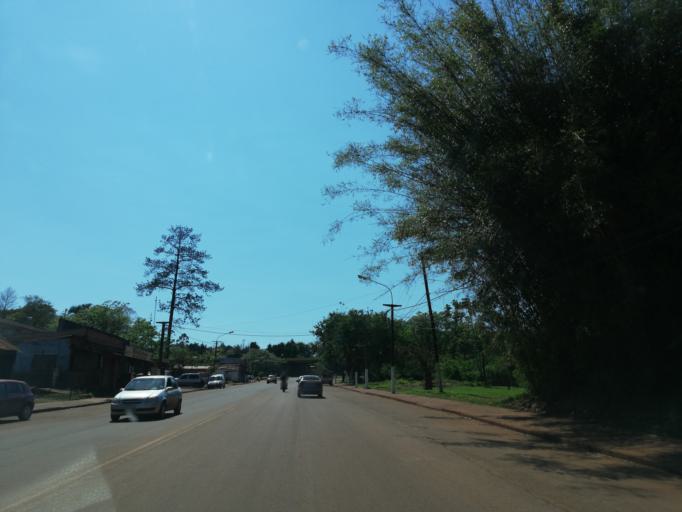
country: AR
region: Misiones
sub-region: Departamento de Eldorado
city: Eldorado
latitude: -26.4035
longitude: -54.6369
